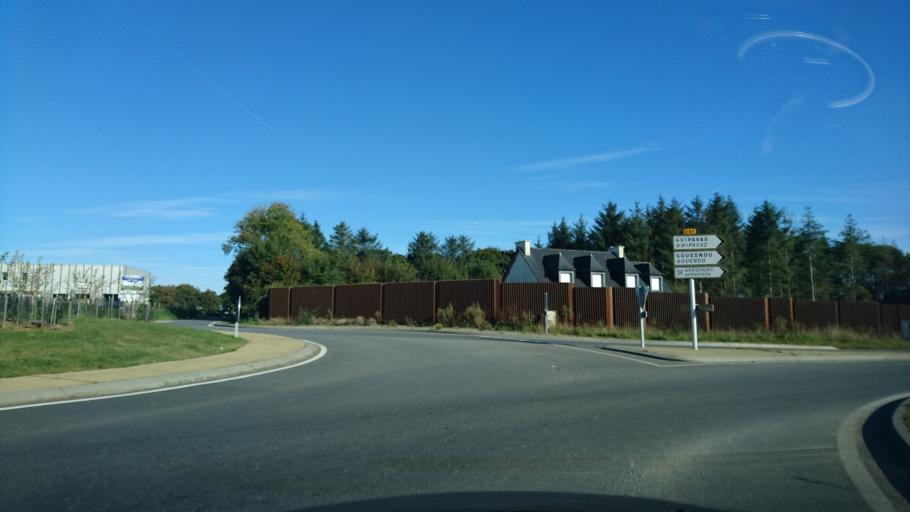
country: FR
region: Brittany
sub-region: Departement du Finistere
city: Bohars
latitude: 48.4494
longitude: -4.5346
